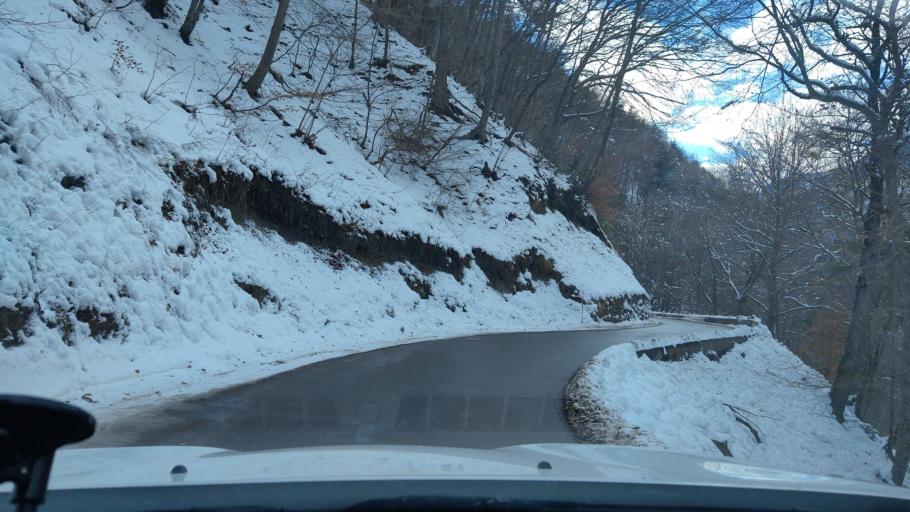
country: FR
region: Rhone-Alpes
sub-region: Departement de la Savoie
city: Salins-les-Thermes
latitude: 45.4501
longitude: 6.5131
